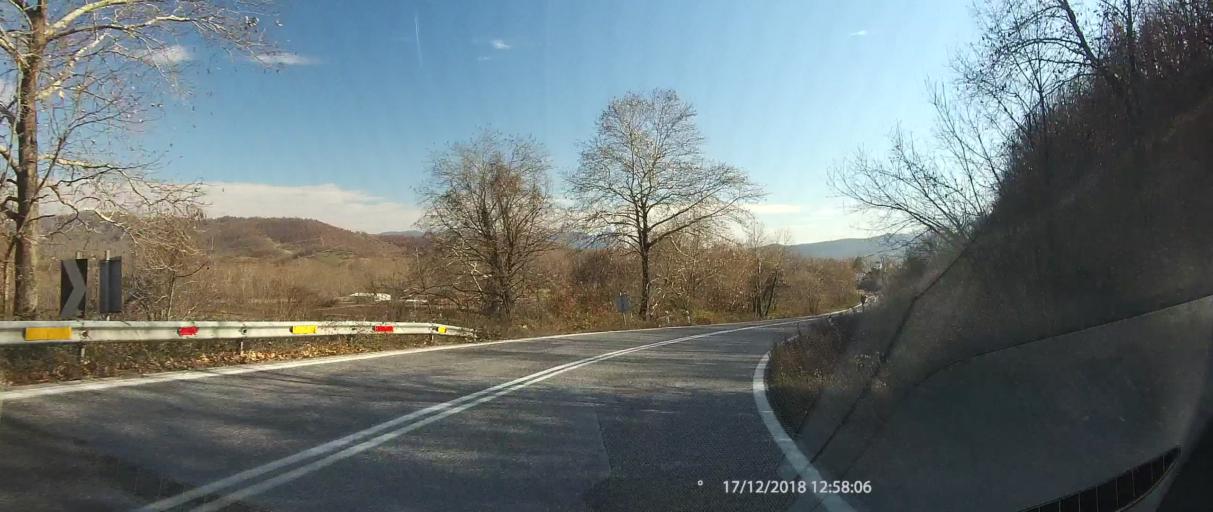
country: GR
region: Thessaly
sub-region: Trikala
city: Kastraki
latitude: 39.7420
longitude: 21.5379
